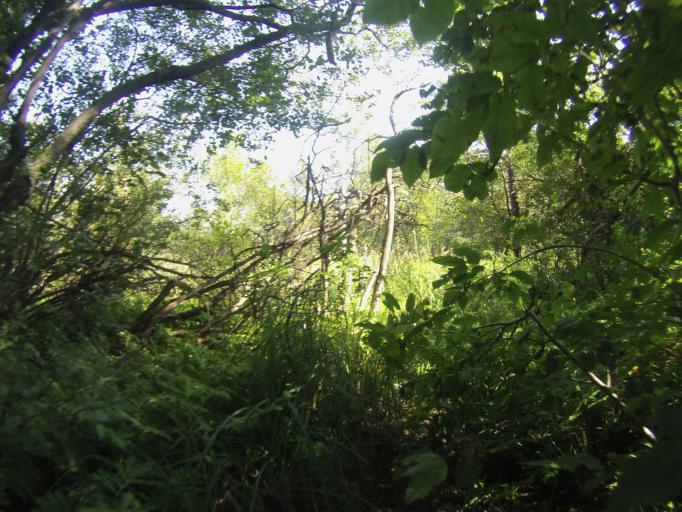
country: CA
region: Ontario
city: Ottawa
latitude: 45.3565
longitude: -75.6148
